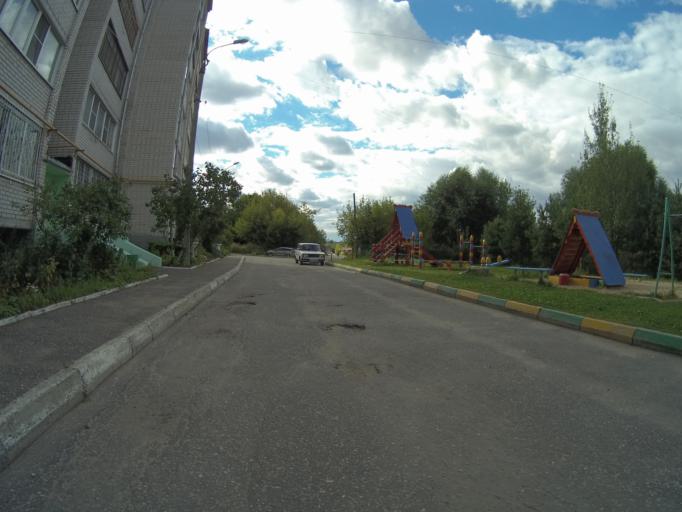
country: RU
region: Vladimir
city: Vladimir
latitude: 56.1209
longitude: 40.3518
